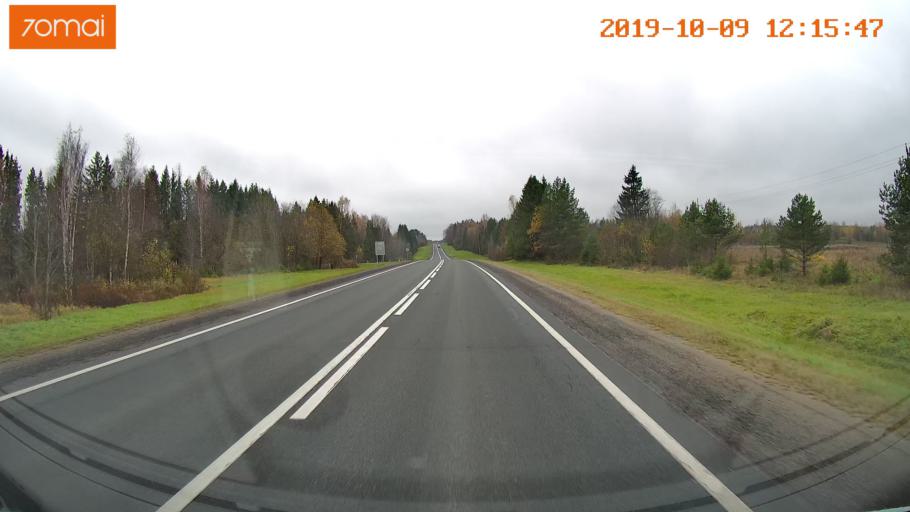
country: RU
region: Jaroslavl
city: Prechistoye
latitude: 58.4782
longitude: 40.3224
